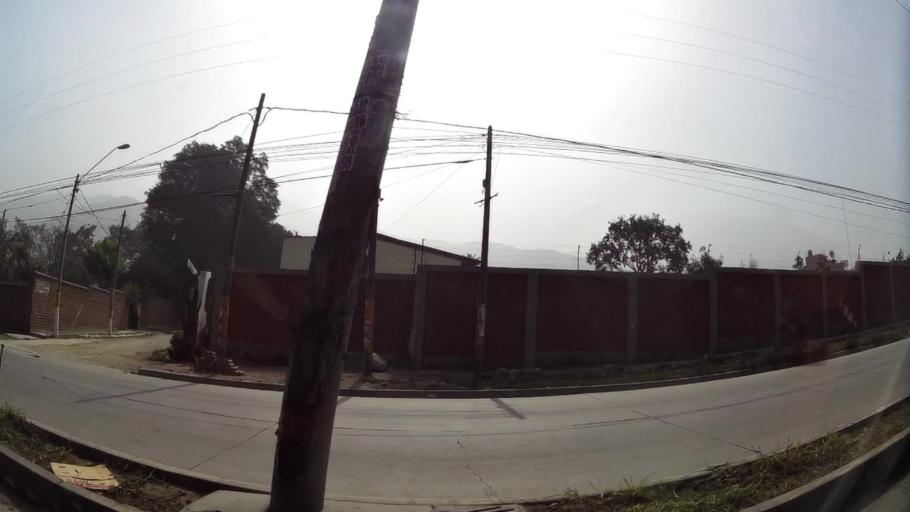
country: PE
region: Lima
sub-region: Lima
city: Chosica
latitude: -11.9468
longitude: -76.7149
